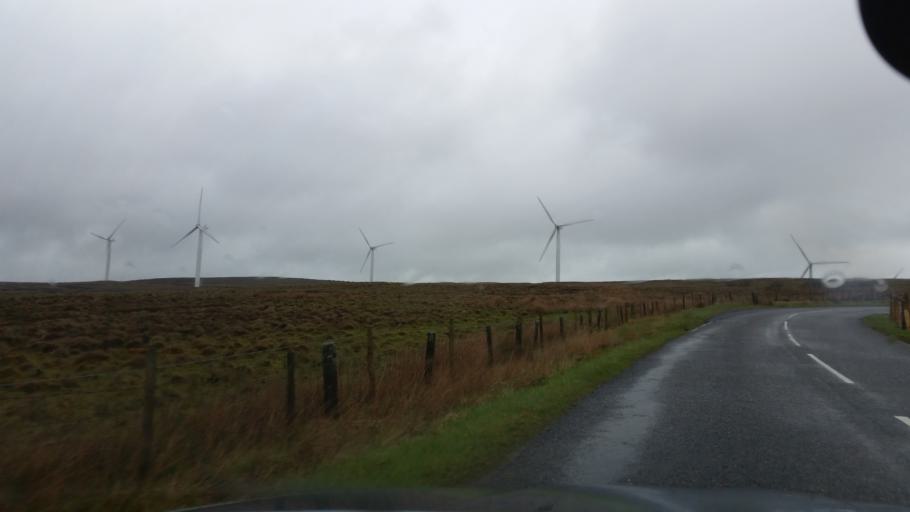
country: GB
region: Northern Ireland
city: Fintona
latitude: 54.4449
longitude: -7.3256
